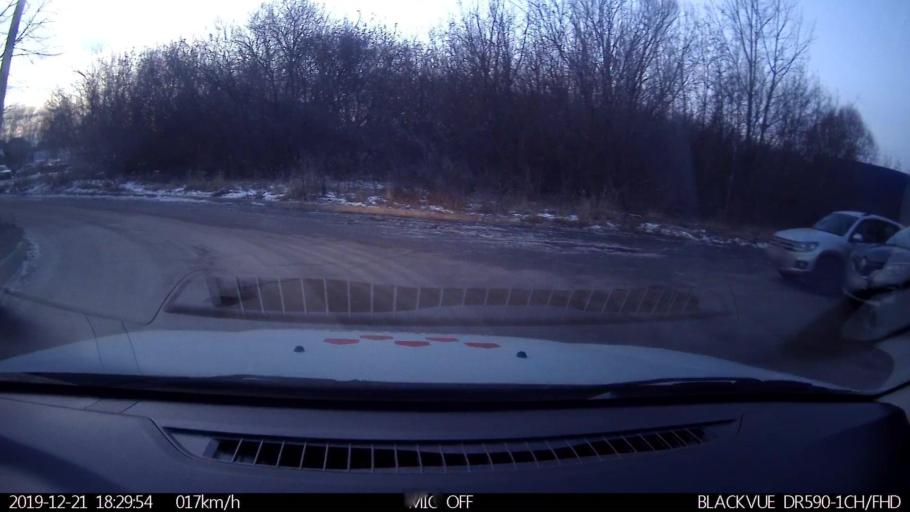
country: RU
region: Nizjnij Novgorod
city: Nizhniy Novgorod
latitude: 56.3364
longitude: 43.9130
